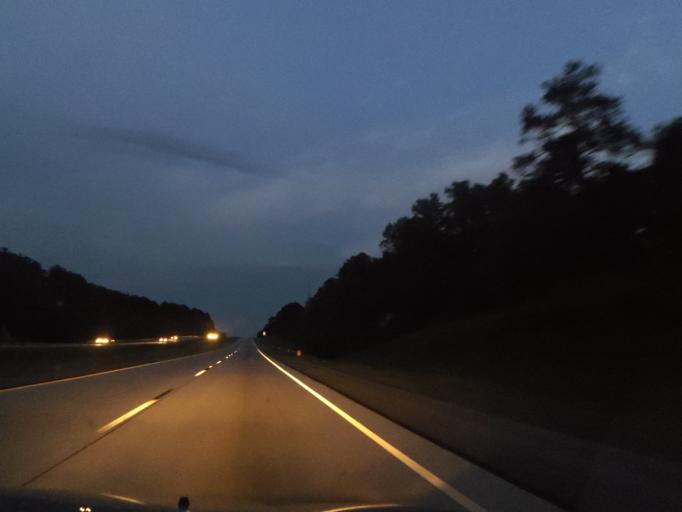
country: US
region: Georgia
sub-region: Columbia County
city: Appling
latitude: 33.5062
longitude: -82.3989
